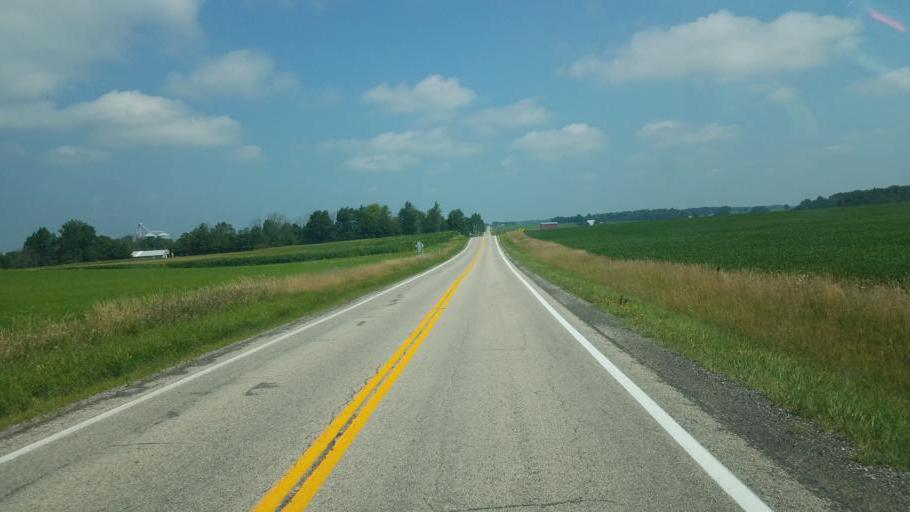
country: US
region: Ohio
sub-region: Crawford County
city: Bucyrus
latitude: 40.8749
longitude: -82.8548
